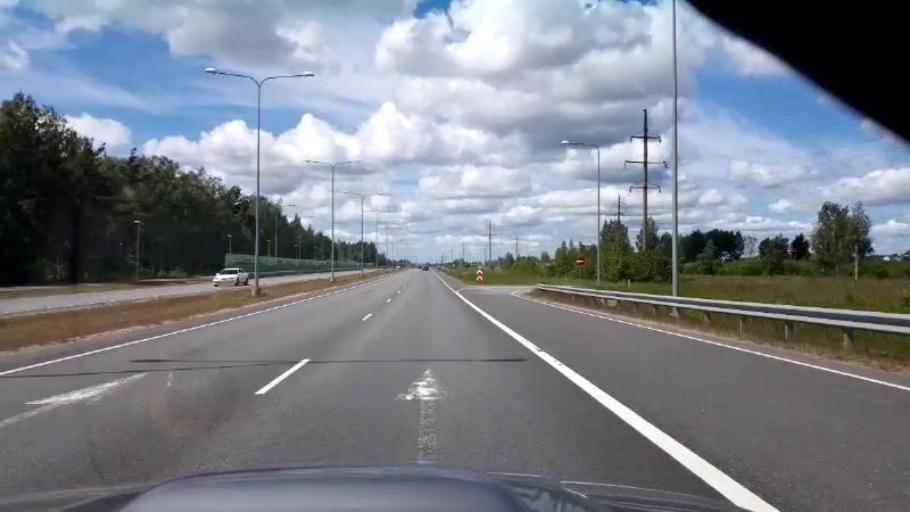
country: EE
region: Paernumaa
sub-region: Paernu linn
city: Parnu
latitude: 58.3893
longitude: 24.5493
